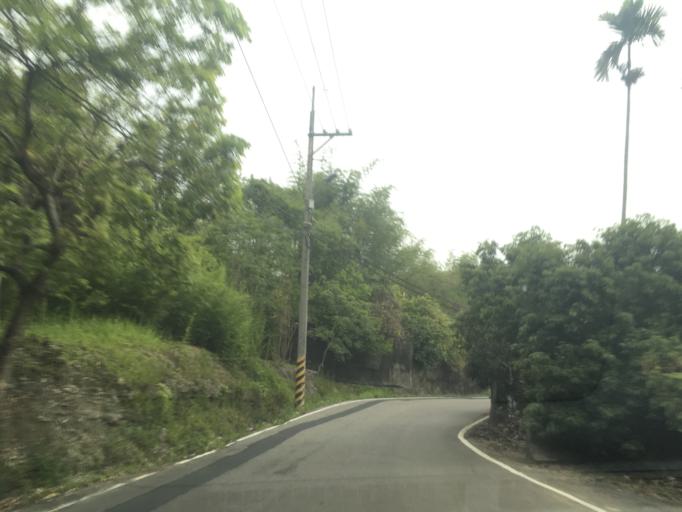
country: TW
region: Taiwan
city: Zhongxing New Village
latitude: 24.0324
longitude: 120.7227
